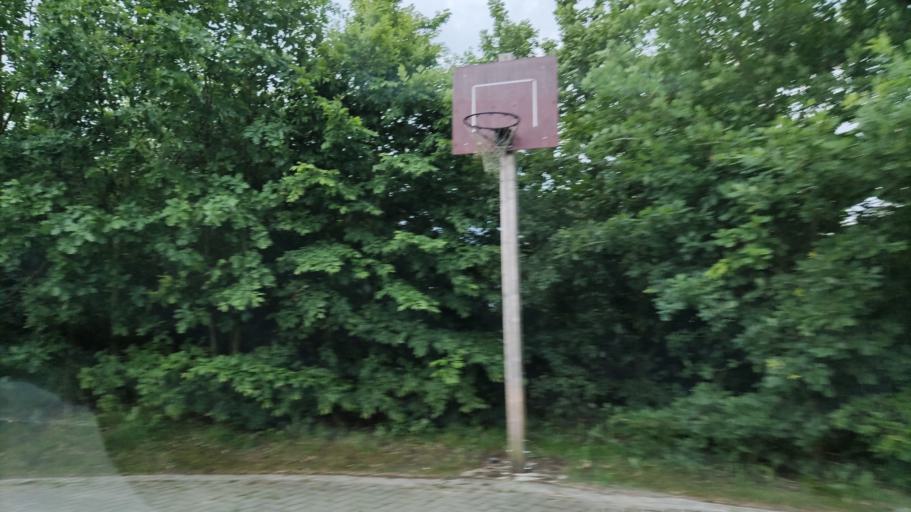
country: DE
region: Lower Saxony
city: Reinstorf
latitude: 53.2721
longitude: 10.5676
